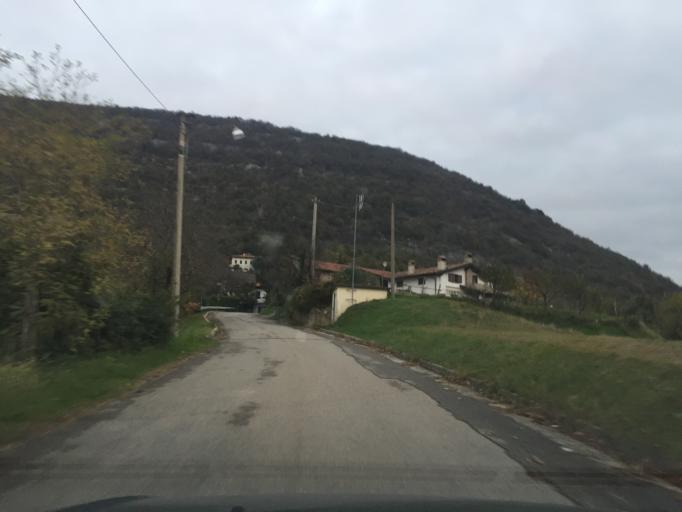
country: SI
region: Nova Gorica
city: Solkan
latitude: 45.9770
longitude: 13.6321
